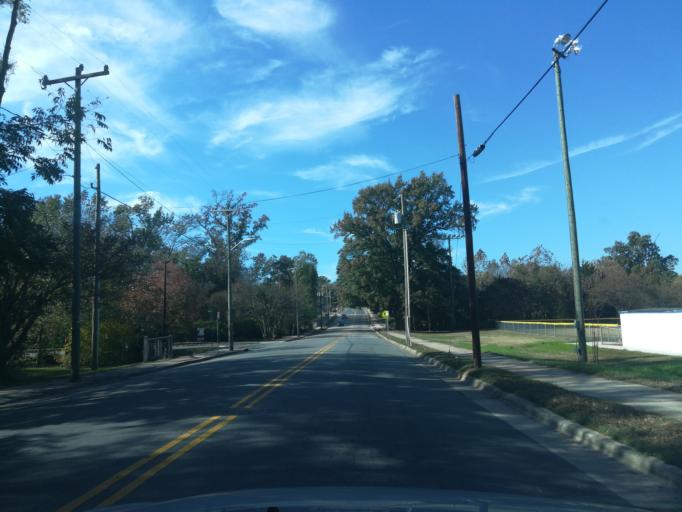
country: US
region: North Carolina
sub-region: Durham County
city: Durham
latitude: 35.9926
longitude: -78.8826
